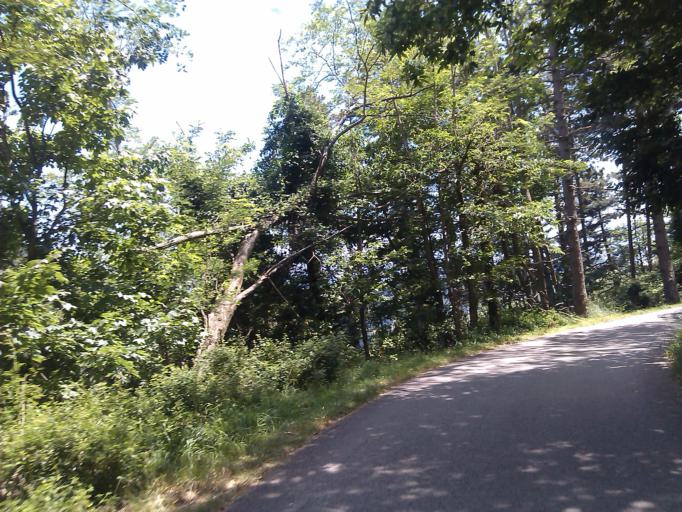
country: IT
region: Tuscany
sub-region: Provincia di Pistoia
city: Montale
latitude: 43.9833
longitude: 11.0413
